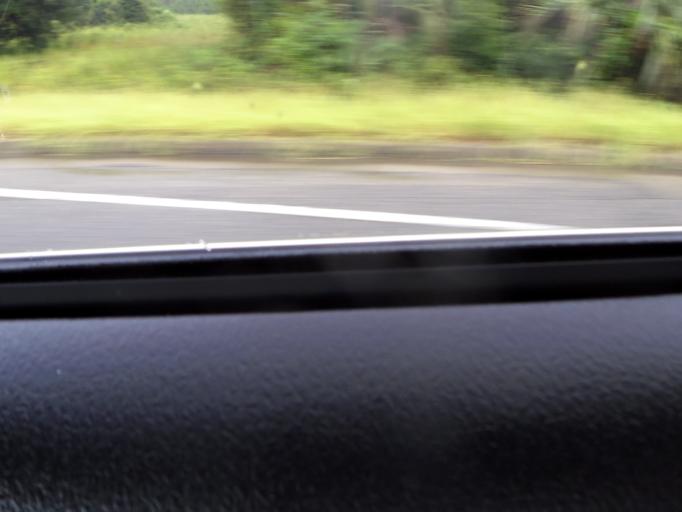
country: US
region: Georgia
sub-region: Wayne County
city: Jesup
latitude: 31.6473
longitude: -81.8557
